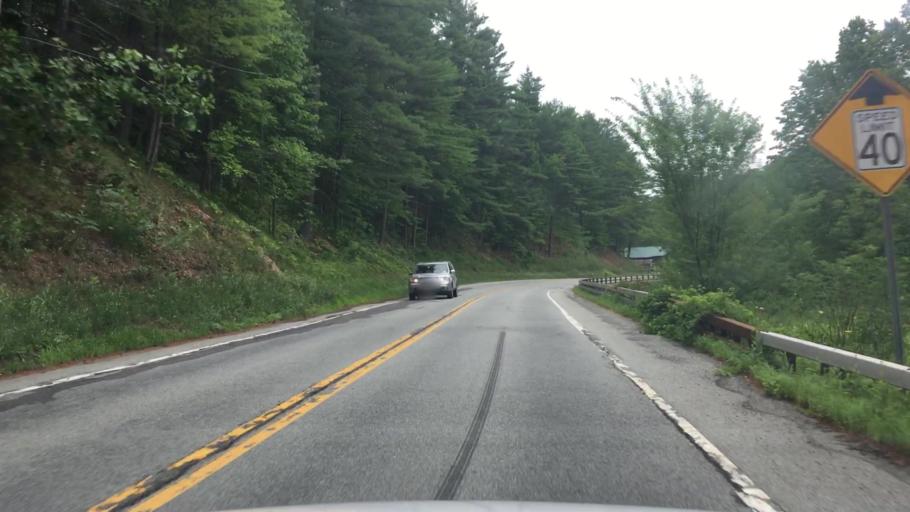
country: US
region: New York
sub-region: Essex County
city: Keeseville
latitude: 44.4268
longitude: -73.6800
